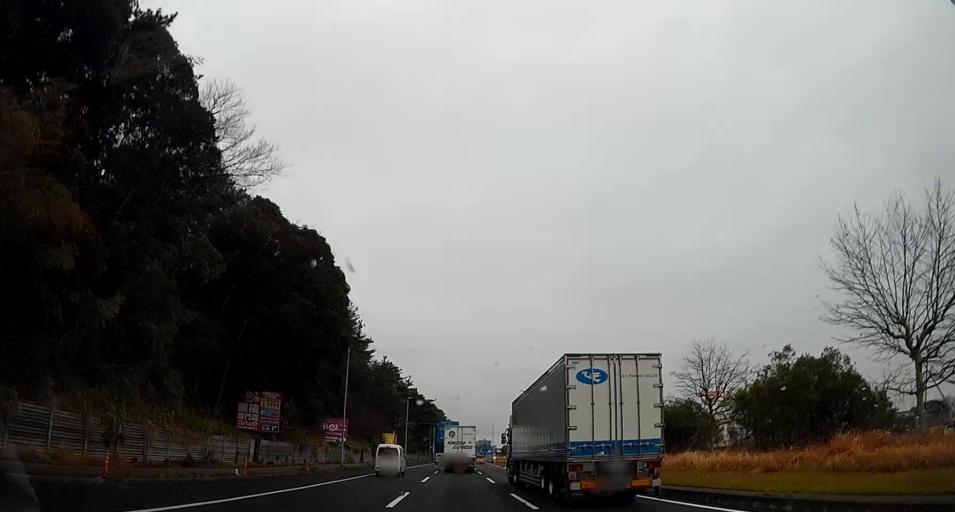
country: JP
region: Chiba
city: Chiba
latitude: 35.6316
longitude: 140.0855
